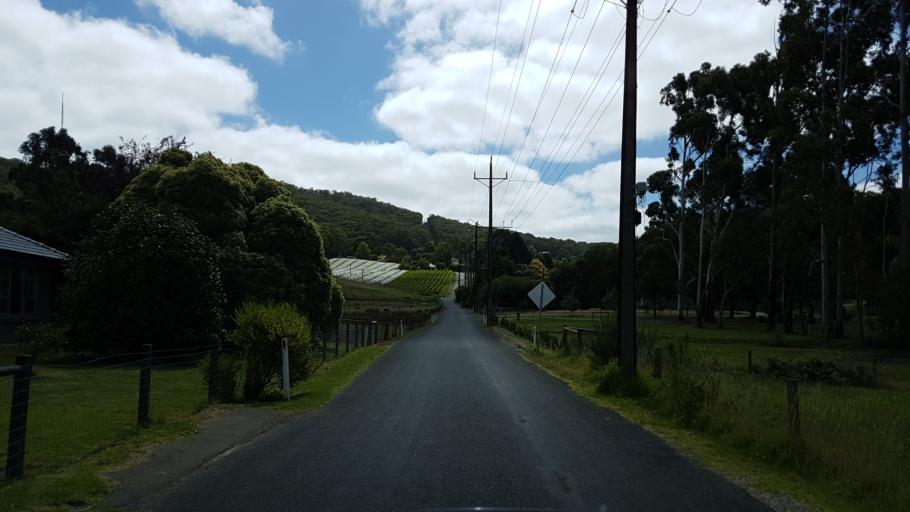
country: AU
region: South Australia
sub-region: Adelaide Hills
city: Crafers
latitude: -34.9830
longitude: 138.7223
